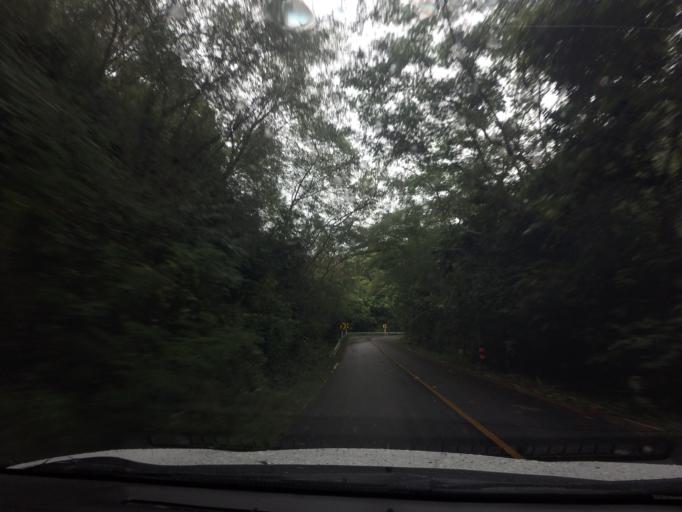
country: TH
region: Rayong
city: Ban Chang
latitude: 12.7639
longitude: 100.9530
